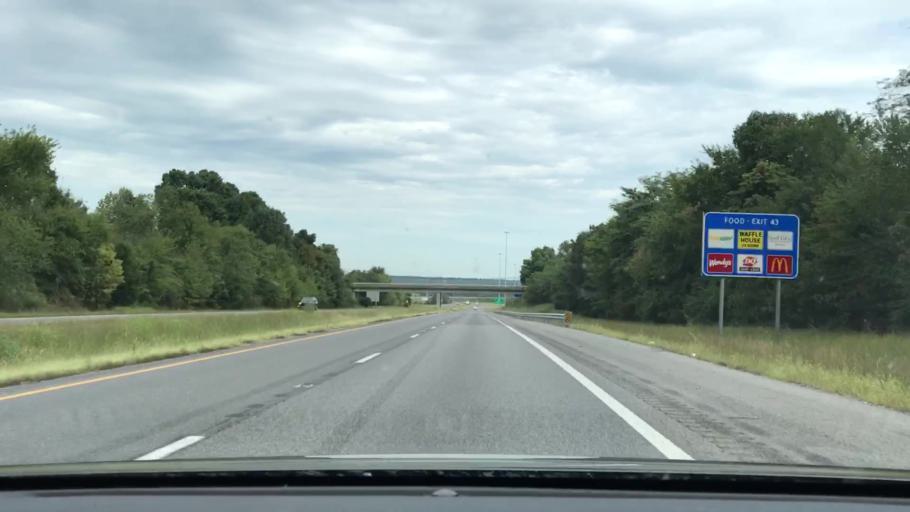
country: US
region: Kentucky
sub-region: Marshall County
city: Benton
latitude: 36.8590
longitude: -88.3673
